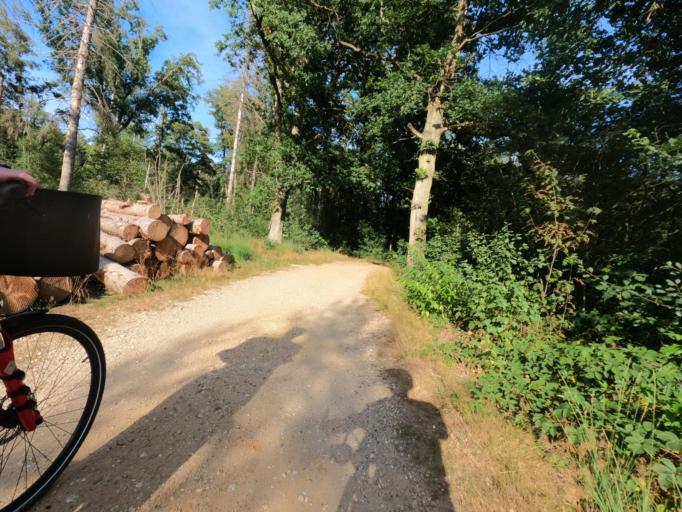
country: NL
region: Limburg
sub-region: Gemeente Beesel
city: Offenbeek
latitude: 51.2272
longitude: 6.0981
